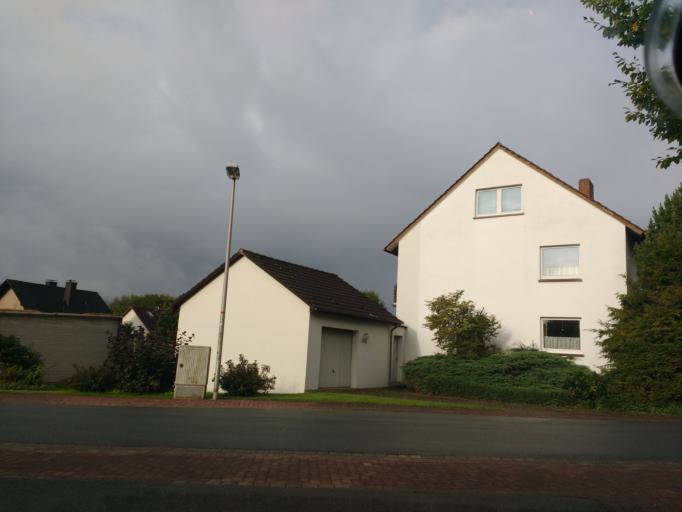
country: DE
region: North Rhine-Westphalia
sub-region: Regierungsbezirk Detmold
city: Barntrup
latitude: 51.9890
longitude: 9.1211
